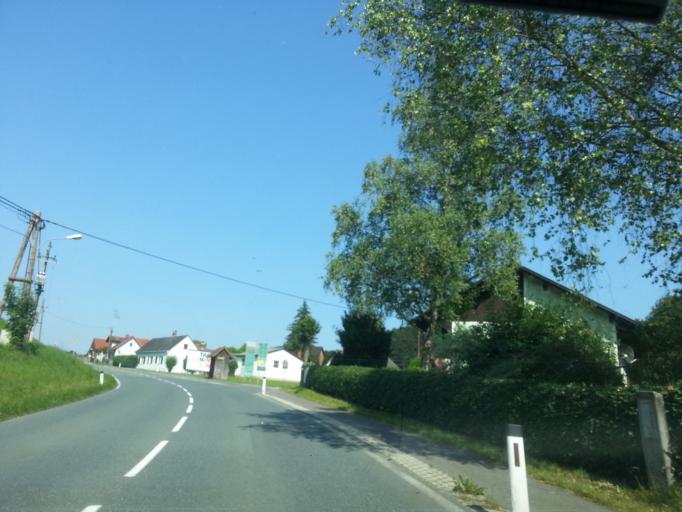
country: AT
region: Styria
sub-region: Politischer Bezirk Leibnitz
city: Grossklein
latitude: 46.7341
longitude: 15.4514
